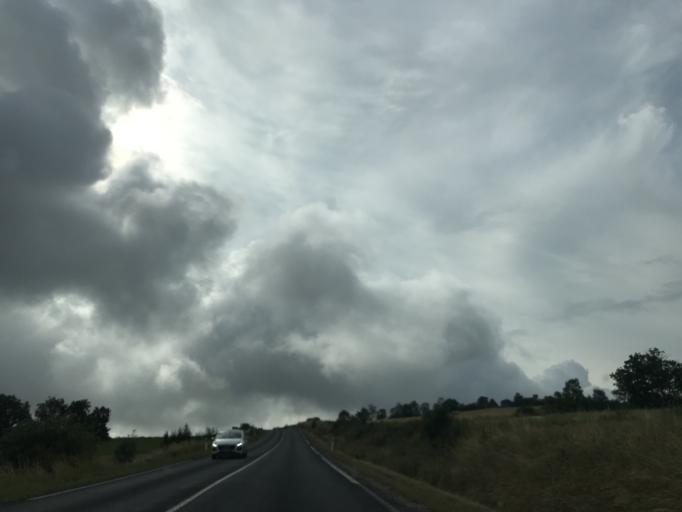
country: FR
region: Auvergne
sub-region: Departement de la Haute-Loire
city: Polignac
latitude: 45.0814
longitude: 3.8235
